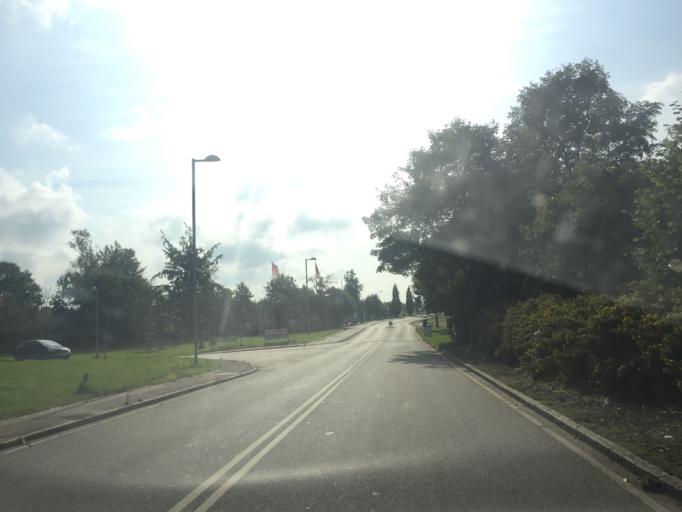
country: DK
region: Zealand
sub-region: Holbaek Kommune
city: Tollose
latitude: 55.6146
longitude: 11.7849
